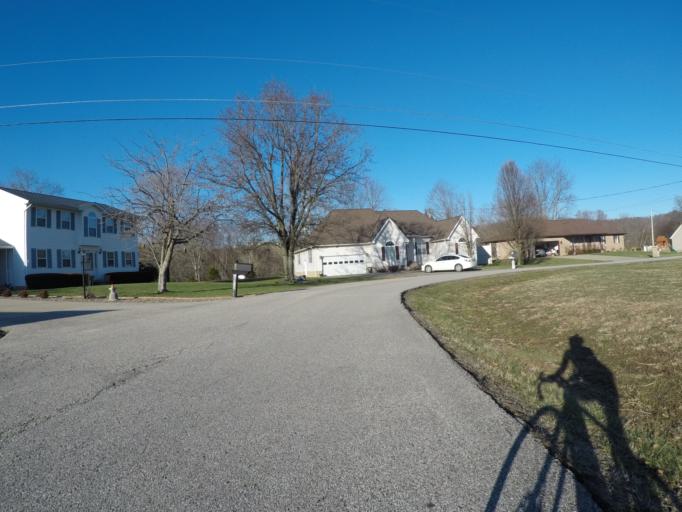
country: US
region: West Virginia
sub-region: Cabell County
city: Huntington
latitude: 38.4605
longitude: -82.4404
